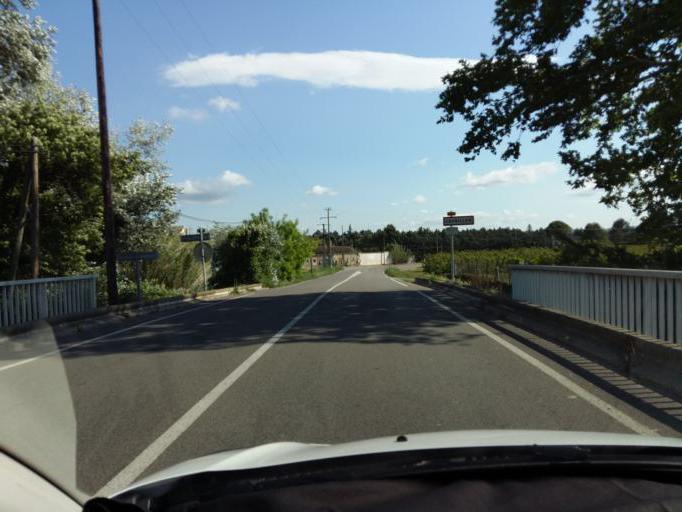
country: FR
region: Provence-Alpes-Cote d'Azur
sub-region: Departement du Vaucluse
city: Cavaillon
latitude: 43.8490
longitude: 5.0603
